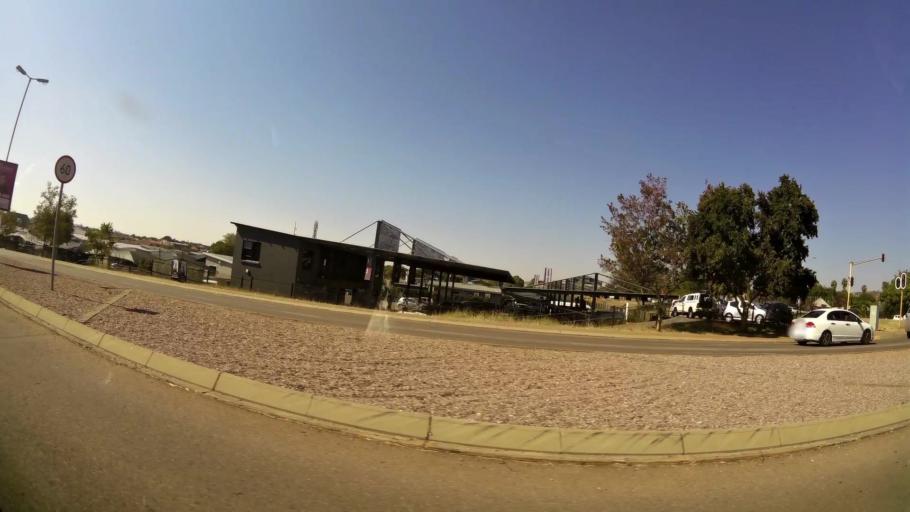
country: ZA
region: Gauteng
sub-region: City of Tshwane Metropolitan Municipality
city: Pretoria
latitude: -25.6807
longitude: 28.2650
